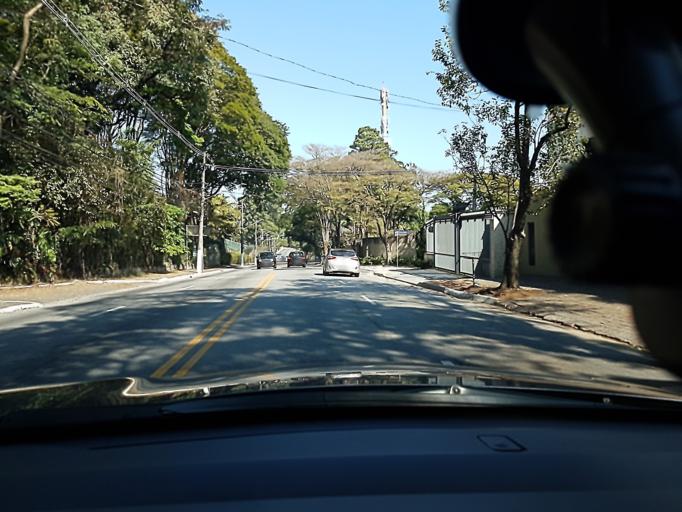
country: BR
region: Sao Paulo
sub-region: Taboao Da Serra
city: Taboao da Serra
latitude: -23.6054
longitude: -46.7125
